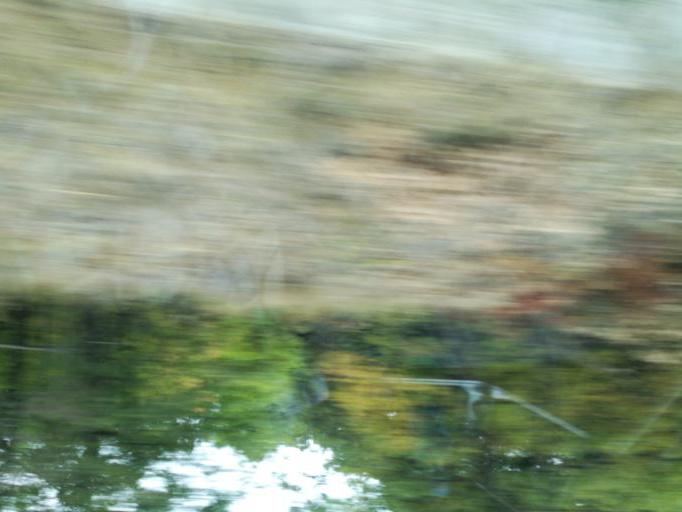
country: RO
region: Tulcea
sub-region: Comuna Horia
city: Horia
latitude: 44.9960
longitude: 28.4509
